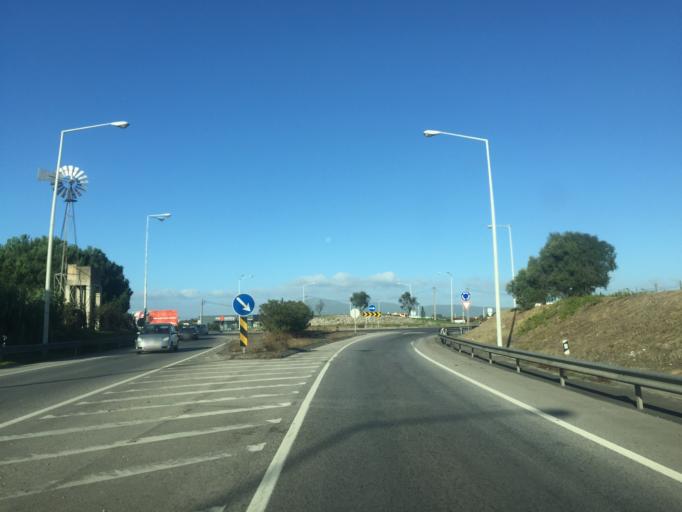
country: PT
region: Lisbon
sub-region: Azambuja
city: Aveiras de Cima
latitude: 39.1450
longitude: -8.9007
